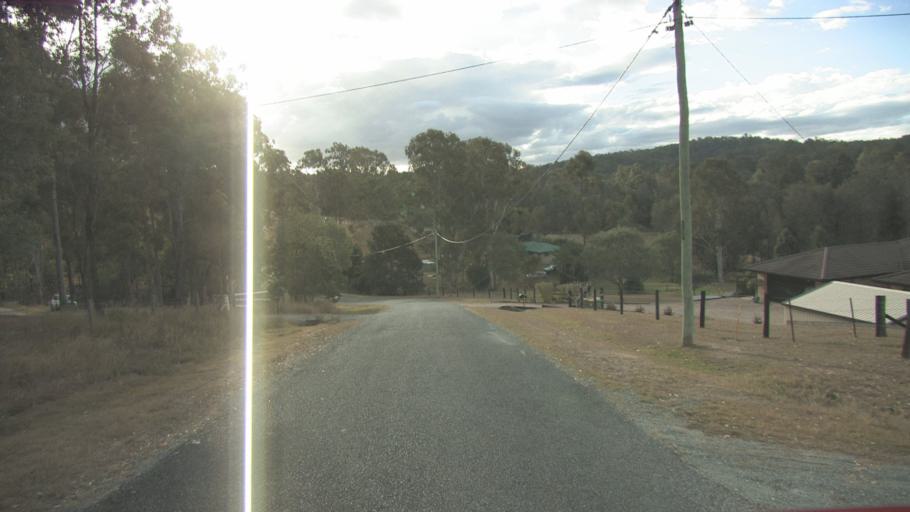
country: AU
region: Queensland
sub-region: Logan
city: Cedar Vale
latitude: -27.9319
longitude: 153.0666
